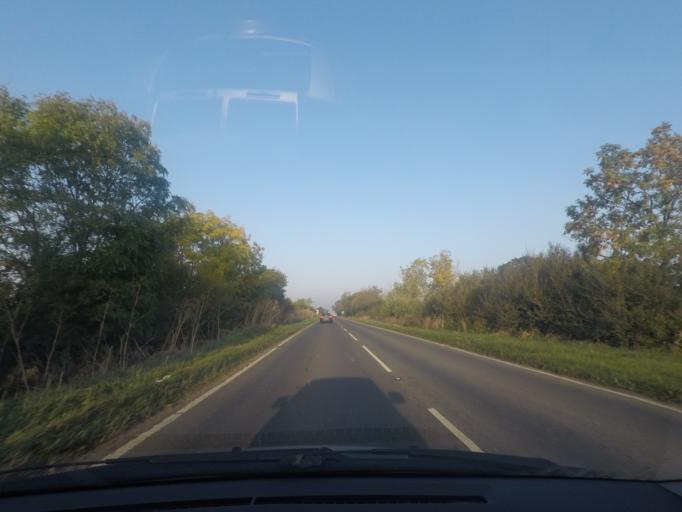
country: GB
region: England
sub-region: City of York
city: Nether Poppleton
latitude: 53.9813
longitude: -1.2018
